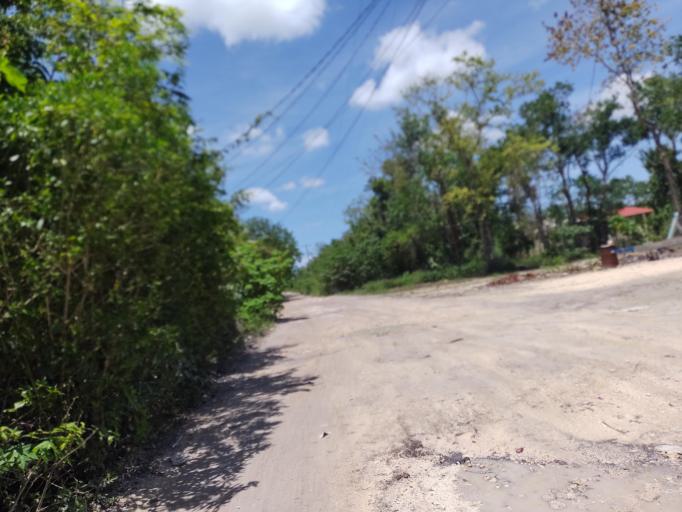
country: MX
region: Quintana Roo
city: San Miguel de Cozumel
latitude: 20.4899
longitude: -86.9077
